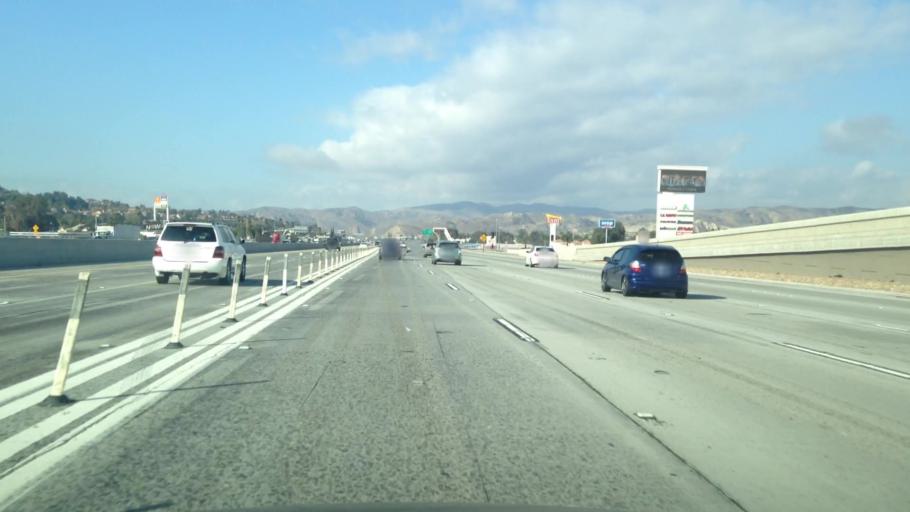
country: US
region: California
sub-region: Riverside County
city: Corona
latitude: 33.8808
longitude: -117.6090
